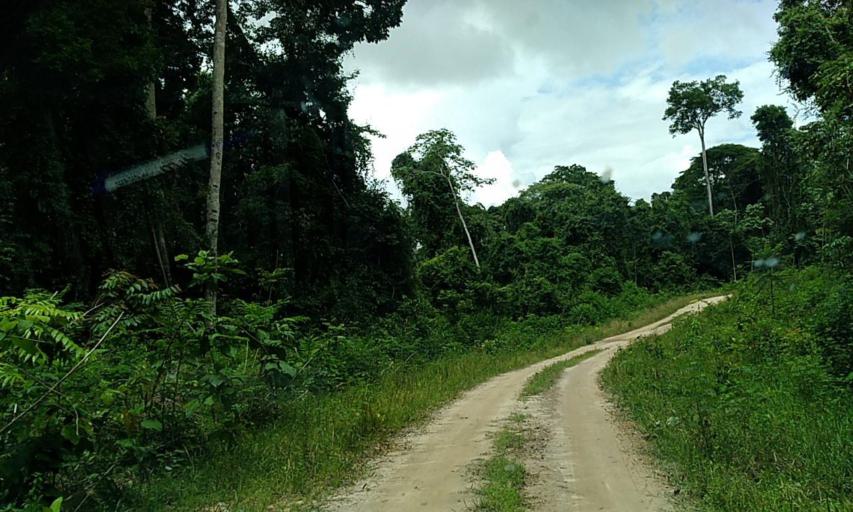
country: BR
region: Para
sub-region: Altamira
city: Altamira
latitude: -3.0557
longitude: -52.9095
